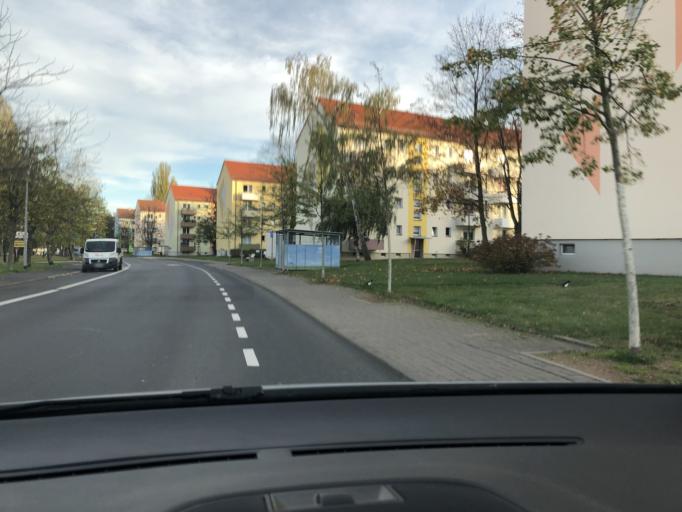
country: DE
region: Thuringia
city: Ilmenau
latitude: 50.6772
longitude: 10.9234
